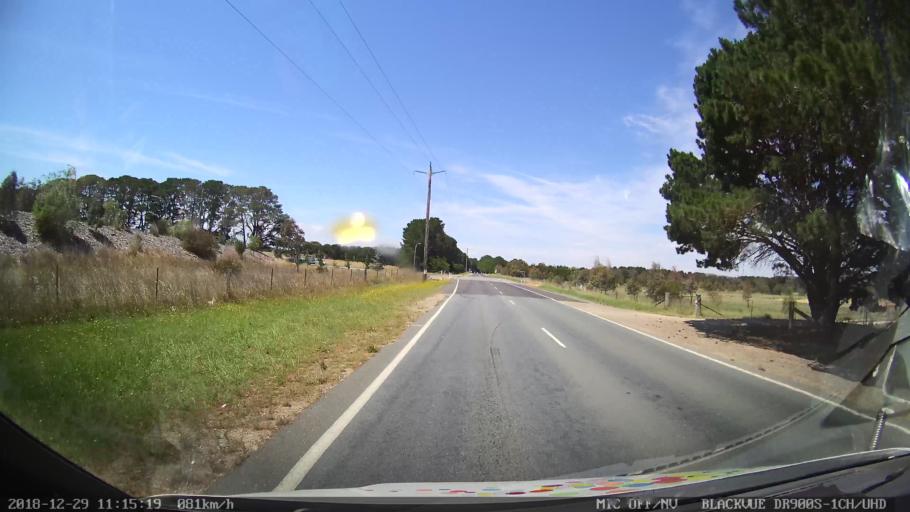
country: AU
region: New South Wales
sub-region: Palerang
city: Bungendore
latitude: -35.2369
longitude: 149.4444
